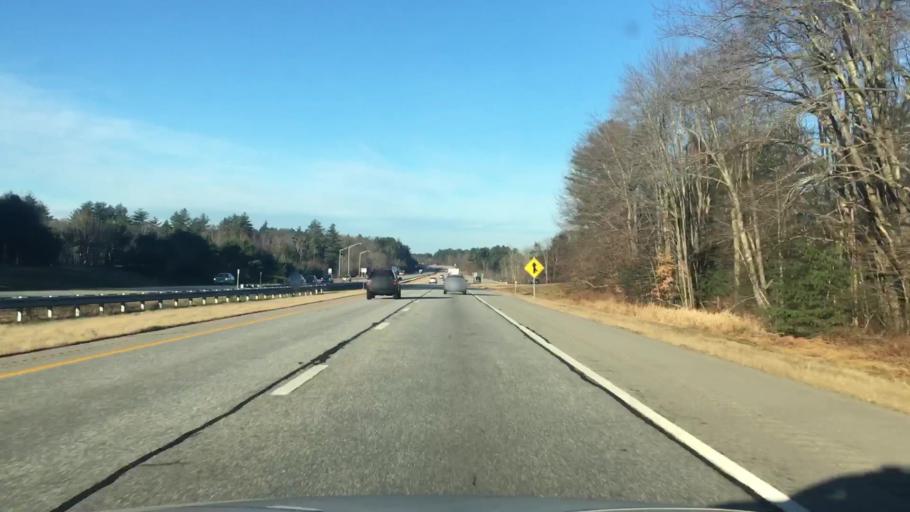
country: US
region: New Hampshire
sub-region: Rockingham County
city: Epping
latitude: 43.0272
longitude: -71.1177
